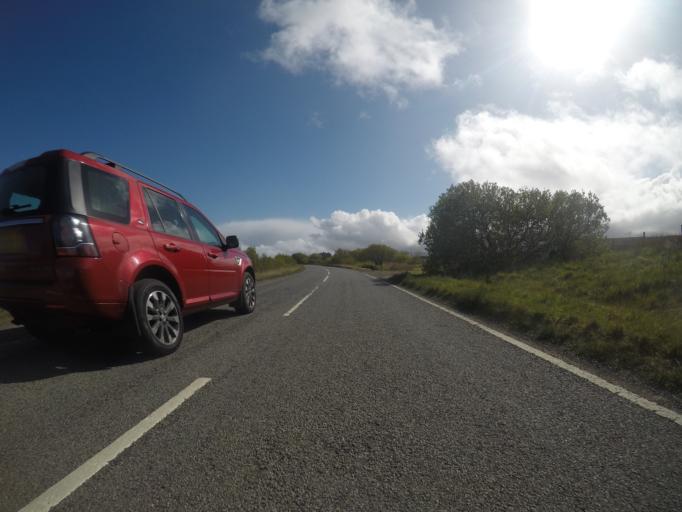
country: GB
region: Scotland
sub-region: Highland
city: Portree
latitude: 57.5927
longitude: -6.1597
